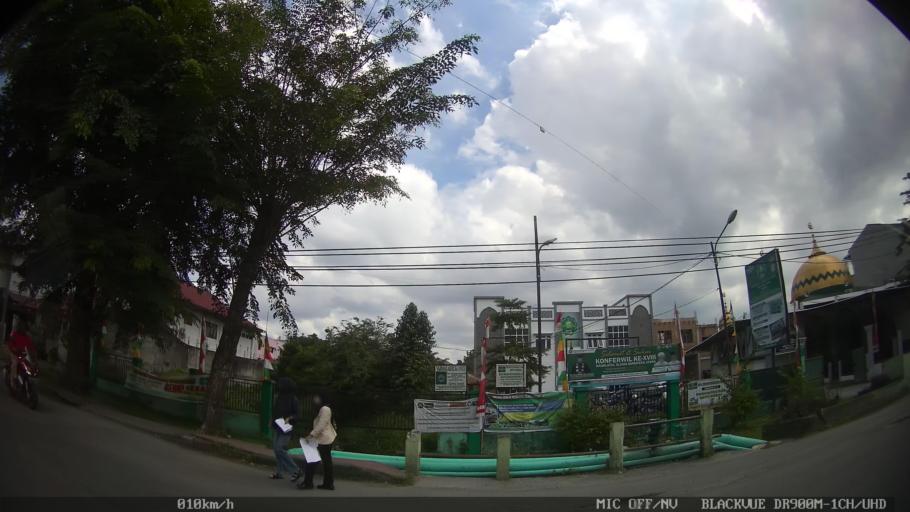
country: ID
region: North Sumatra
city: Sunggal
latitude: 3.6053
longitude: 98.6271
